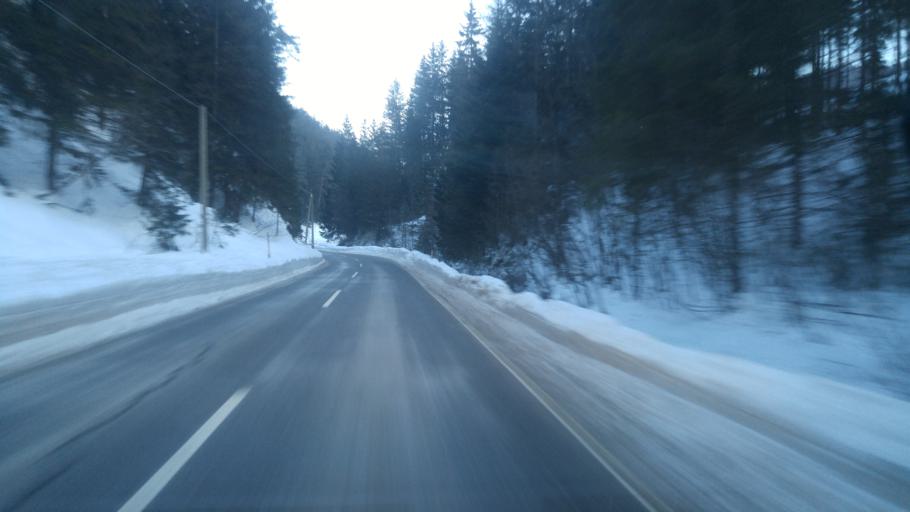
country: AT
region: Lower Austria
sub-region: Politischer Bezirk Wiener Neustadt
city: Rohr im Gebirge
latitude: 47.8751
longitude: 15.7799
